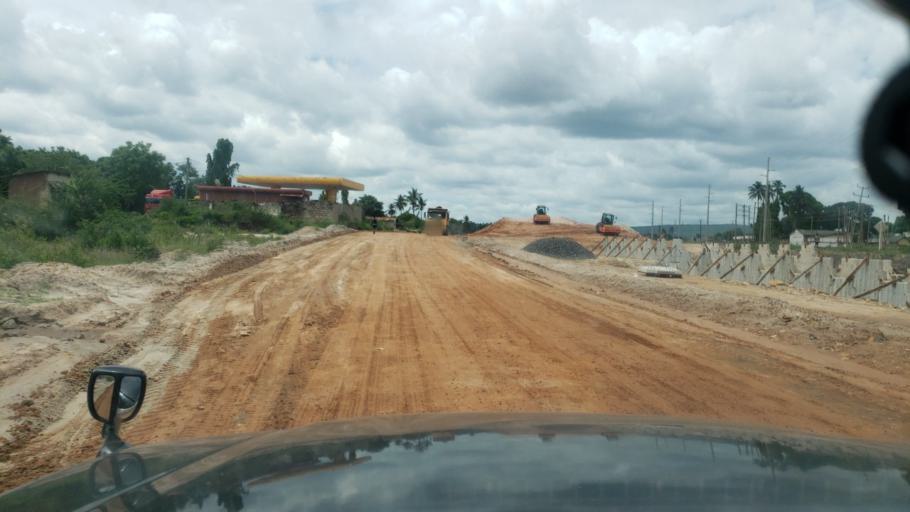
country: TZ
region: Pwani
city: Kisarawe
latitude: -6.8838
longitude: 39.1516
